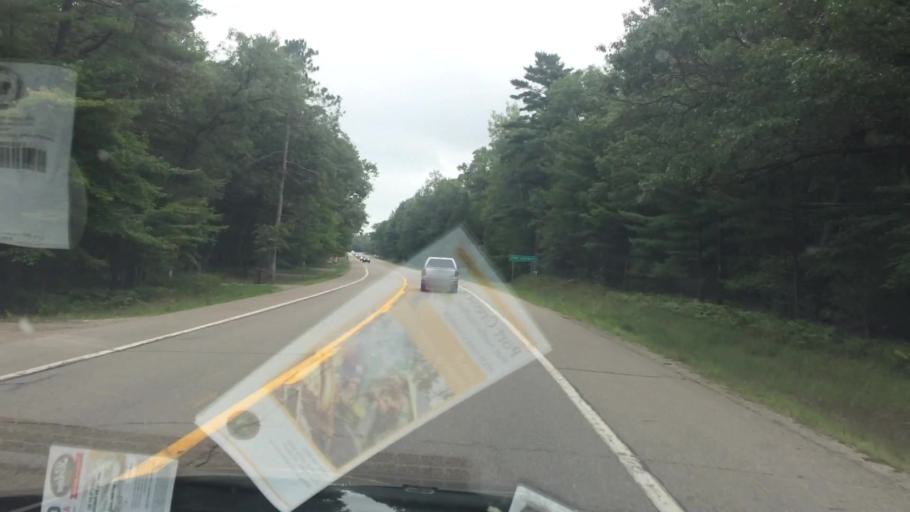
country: US
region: Michigan
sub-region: Huron County
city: Pigeon
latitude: 43.9564
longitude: -83.2647
